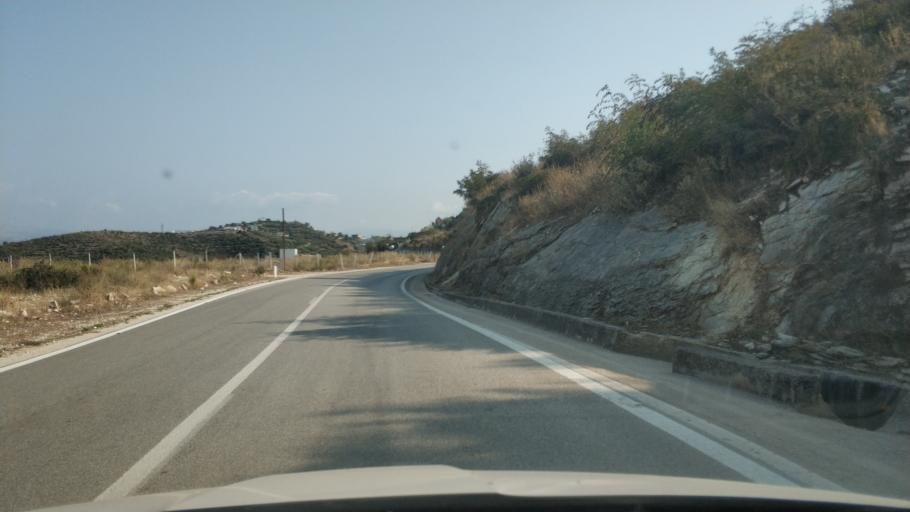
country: AL
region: Vlore
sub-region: Rrethi i Sarandes
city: Sarande
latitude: 39.8857
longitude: 20.0185
